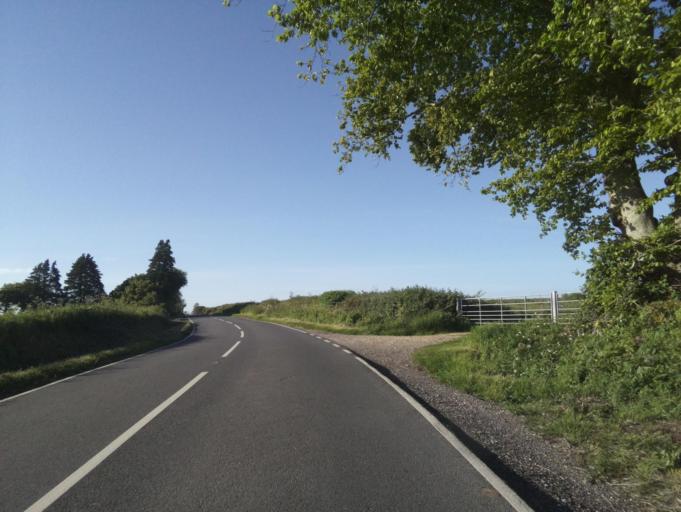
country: GB
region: England
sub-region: Devon
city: Axminster
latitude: 50.7324
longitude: -2.9891
